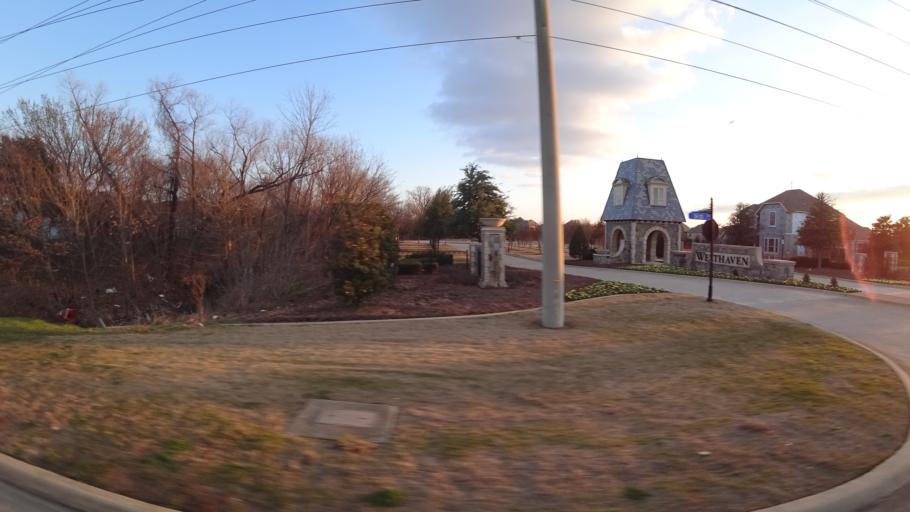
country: US
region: Texas
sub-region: Dallas County
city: Coppell
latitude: 32.9903
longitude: -97.0061
